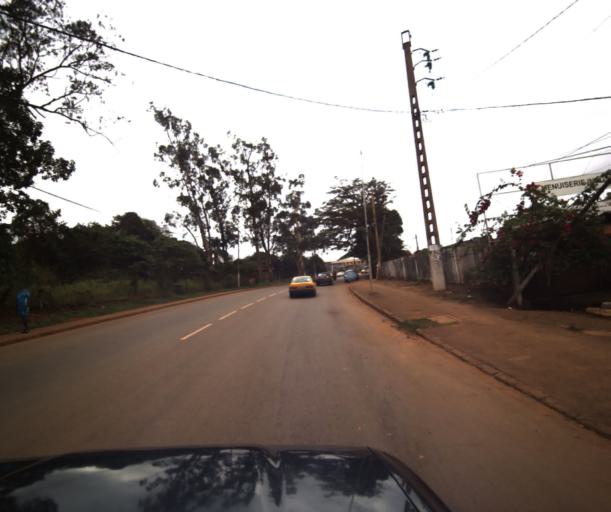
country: CM
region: Centre
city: Yaounde
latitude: 3.8360
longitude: 11.5187
